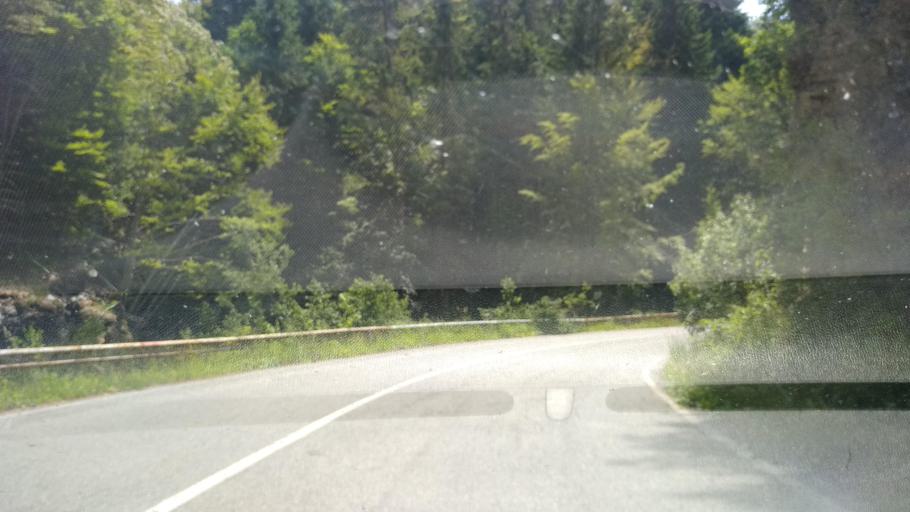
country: RO
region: Hunedoara
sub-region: Comuna Uricani
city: Uricani
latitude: 45.2814
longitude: 22.9668
